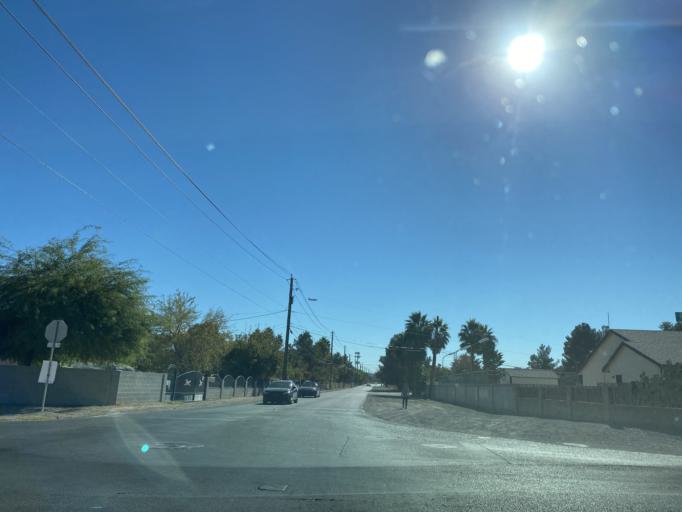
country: US
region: Nevada
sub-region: Clark County
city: Whitney
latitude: 36.0895
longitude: -115.0868
